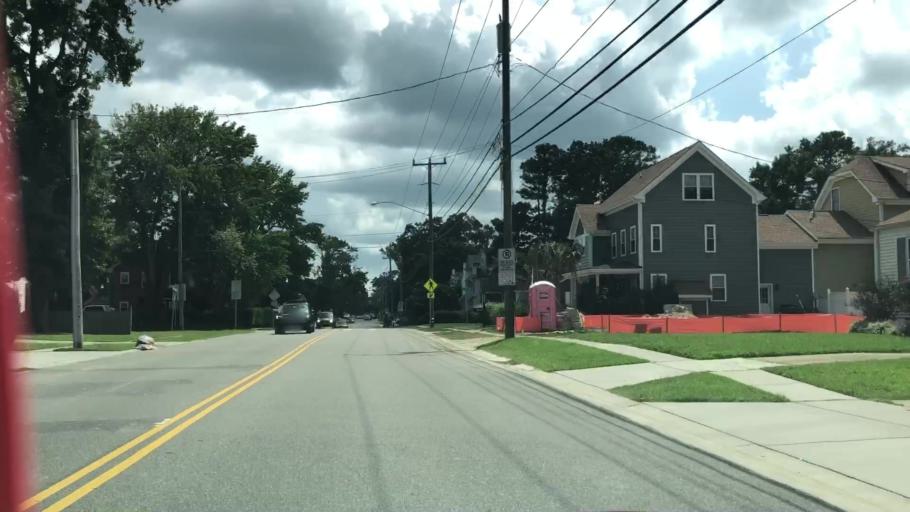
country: US
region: Virginia
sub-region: City of Virginia Beach
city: Virginia Beach
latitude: 36.8402
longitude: -75.9800
